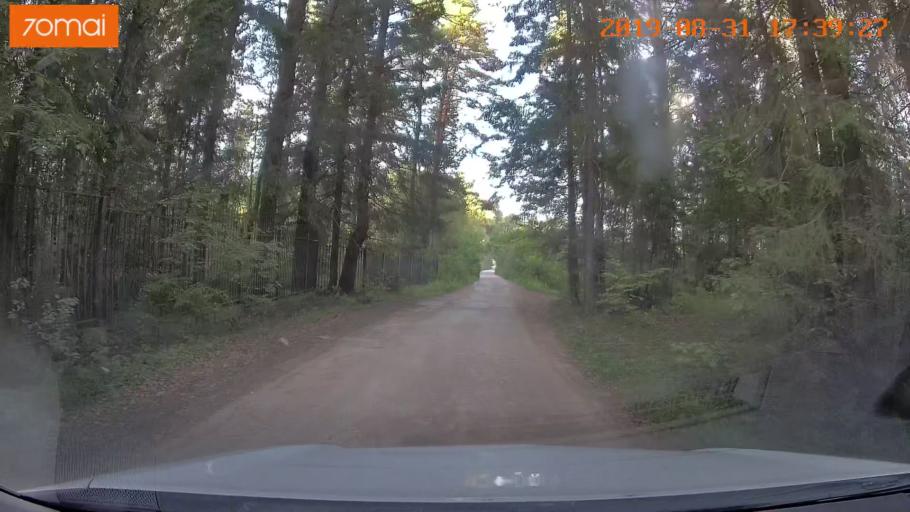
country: RU
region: Kaluga
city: Detchino
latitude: 54.8174
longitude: 36.3632
